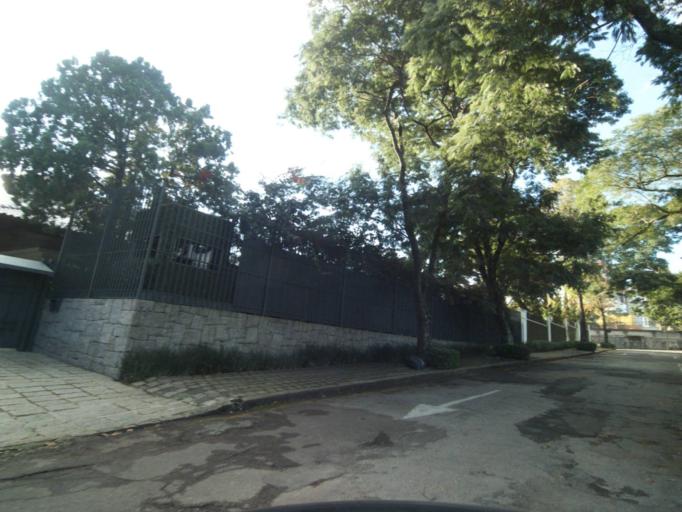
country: BR
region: Parana
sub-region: Curitiba
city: Curitiba
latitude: -25.4212
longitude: -49.2642
